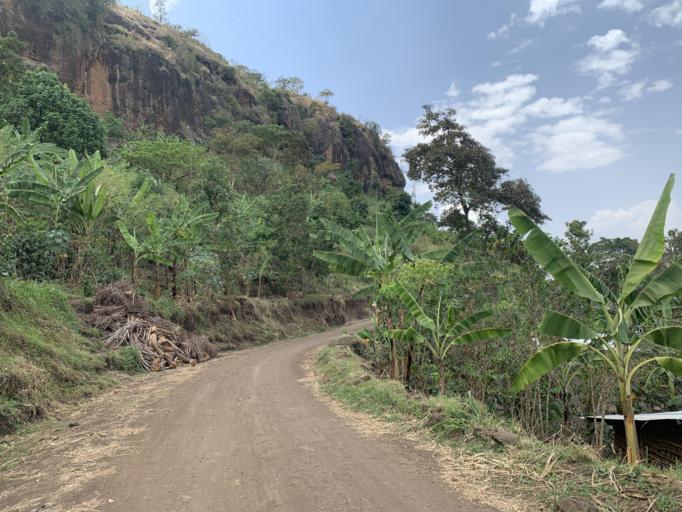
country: UG
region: Eastern Region
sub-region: Sironko District
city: Sironko
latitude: 1.2603
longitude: 34.3045
